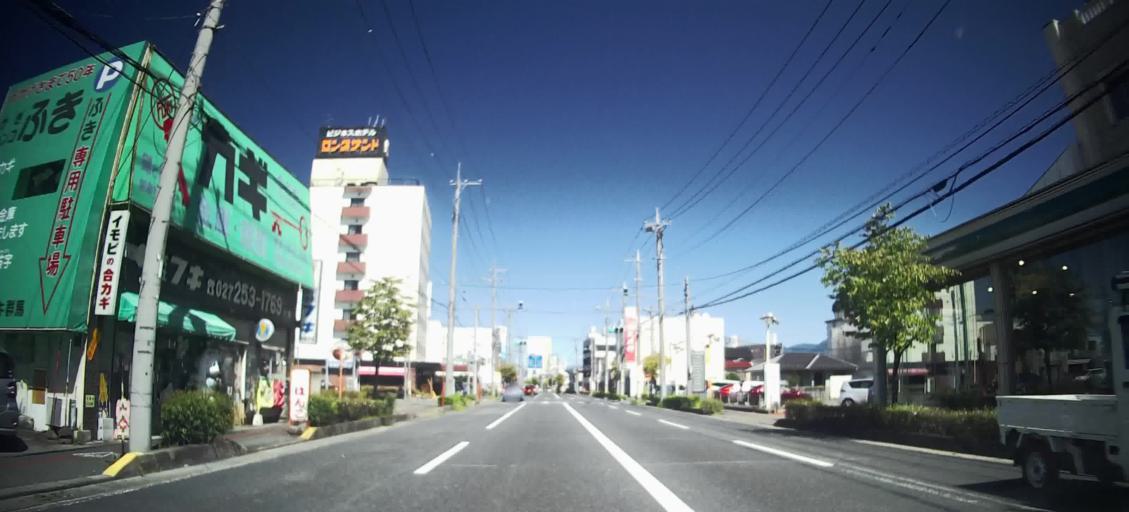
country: JP
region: Gunma
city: Maebashi-shi
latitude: 36.3838
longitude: 139.0538
